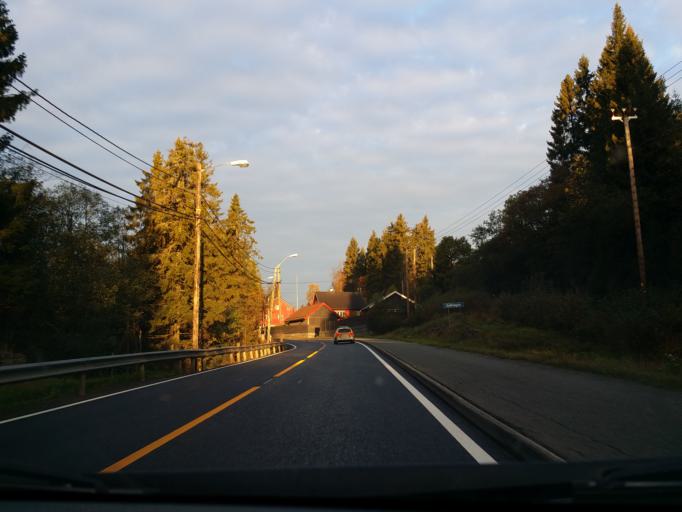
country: NO
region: Akershus
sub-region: Baerum
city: Skui
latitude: 59.9583
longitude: 10.3663
